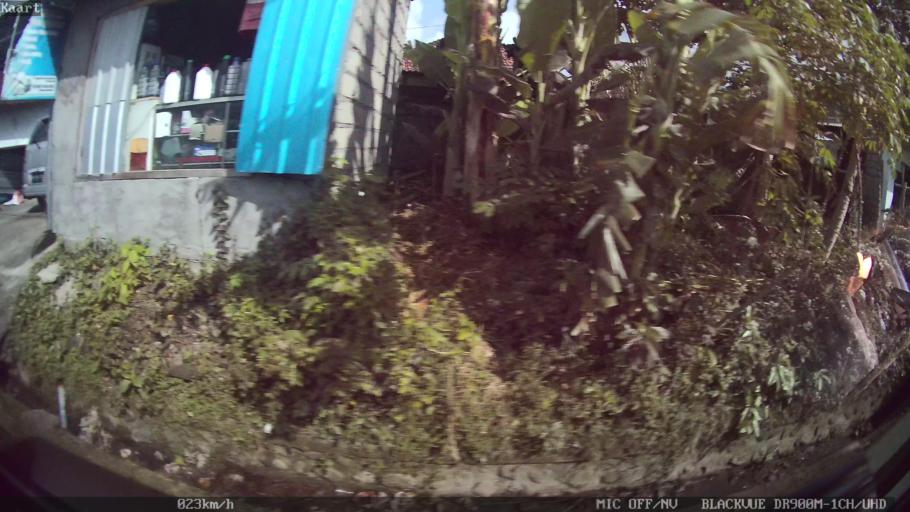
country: ID
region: Bali
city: Banjar Karangsuling
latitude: -8.6087
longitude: 115.2032
